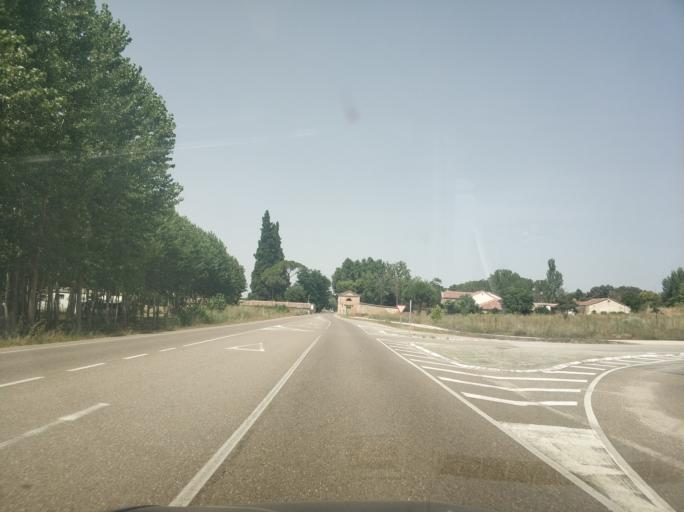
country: ES
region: Castille and Leon
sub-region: Provincia de Salamanca
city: Valverdon
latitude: 41.0409
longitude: -5.7546
